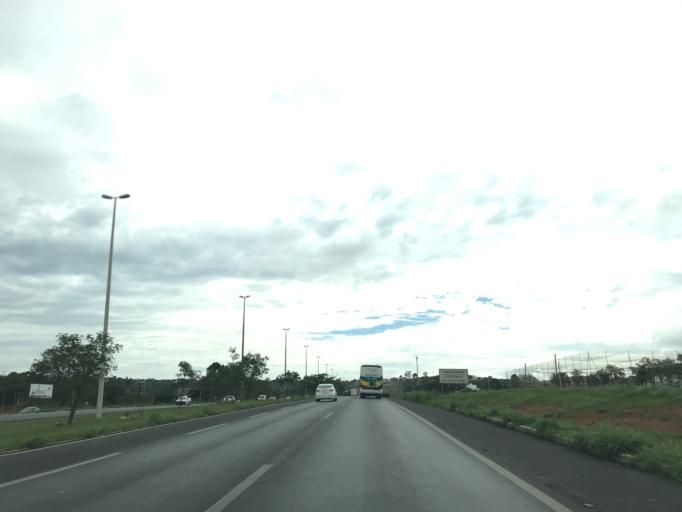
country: BR
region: Federal District
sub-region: Brasilia
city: Brasilia
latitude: -15.6725
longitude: -47.8194
